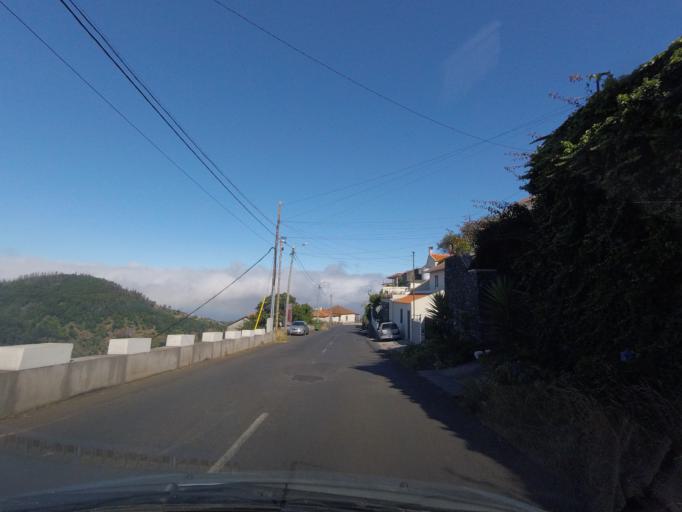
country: PT
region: Madeira
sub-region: Santa Cruz
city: Camacha
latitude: 32.6838
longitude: -16.8482
